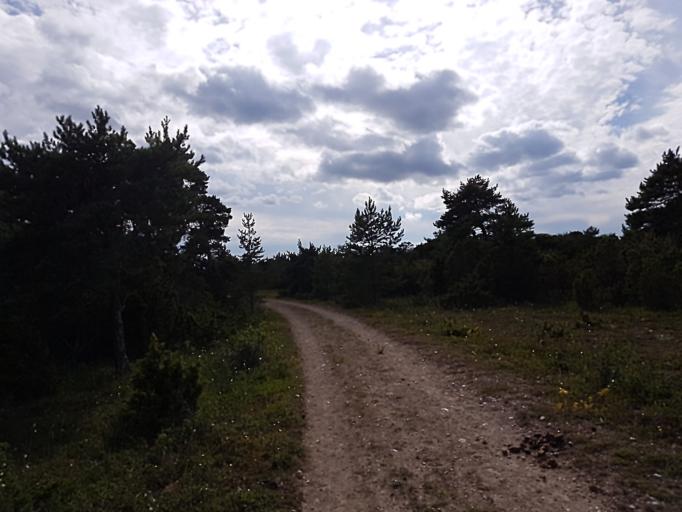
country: SE
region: Gotland
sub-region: Gotland
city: Visby
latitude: 57.6197
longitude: 18.3377
